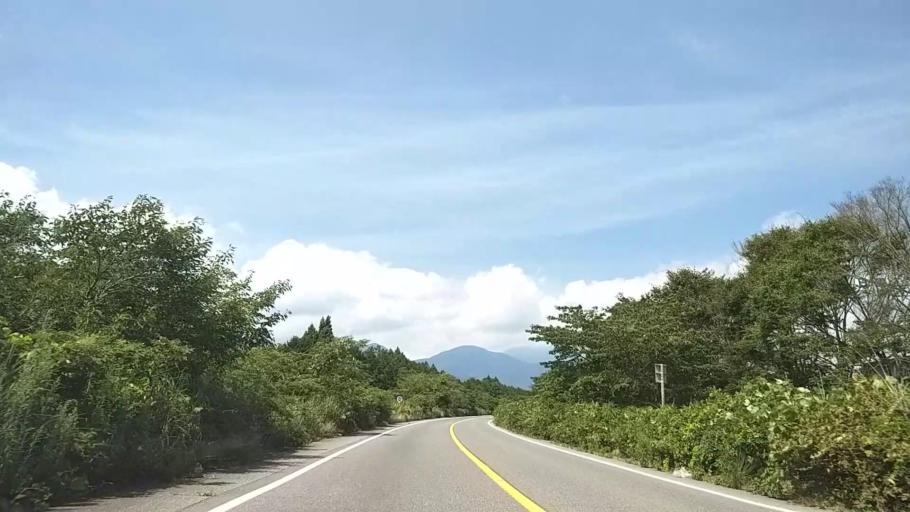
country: JP
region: Shizuoka
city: Fujinomiya
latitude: 35.3175
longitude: 138.5922
